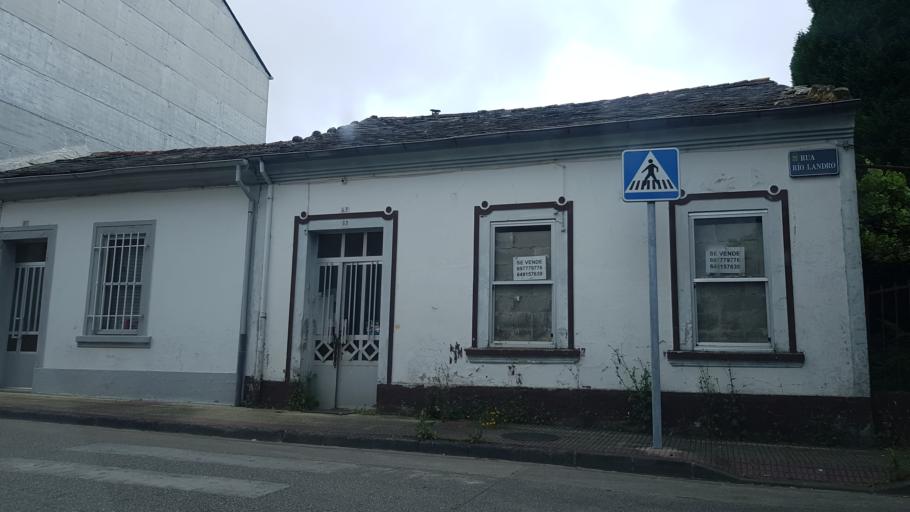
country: ES
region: Galicia
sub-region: Provincia de Lugo
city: Lugo
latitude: 43.0047
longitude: -7.5680
